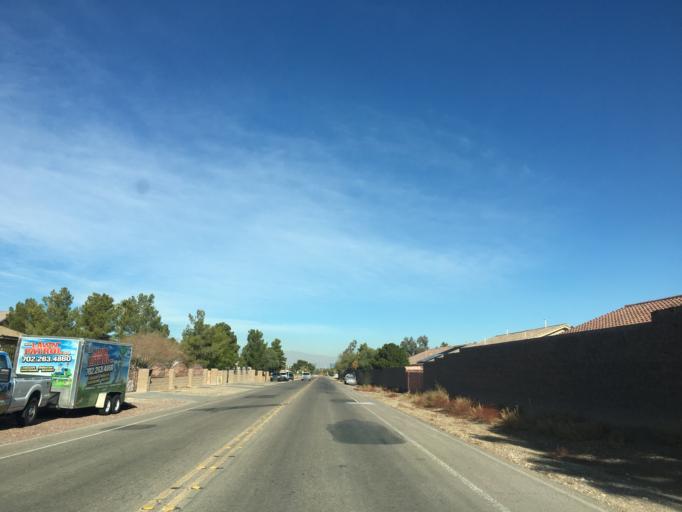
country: US
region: Nevada
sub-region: Clark County
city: Enterprise
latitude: 36.0038
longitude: -115.1659
